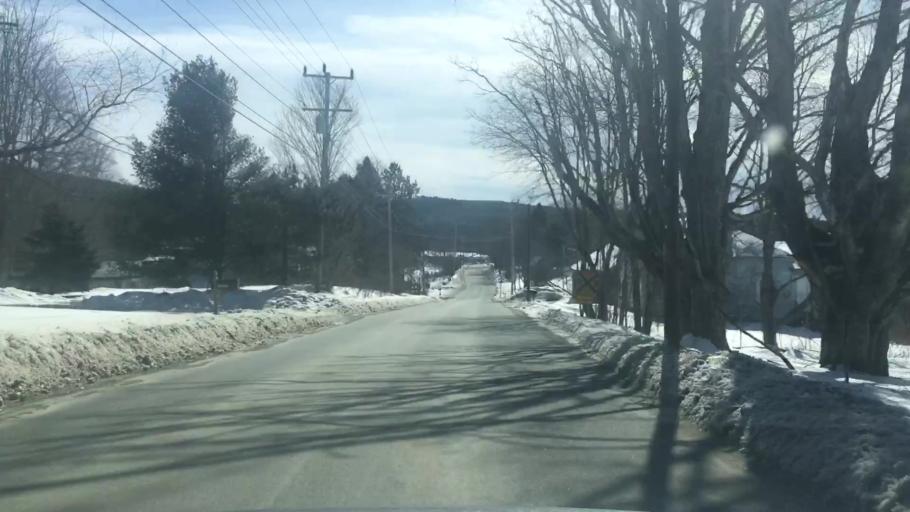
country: US
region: Maine
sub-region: Penobscot County
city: Holden
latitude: 44.7409
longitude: -68.6290
